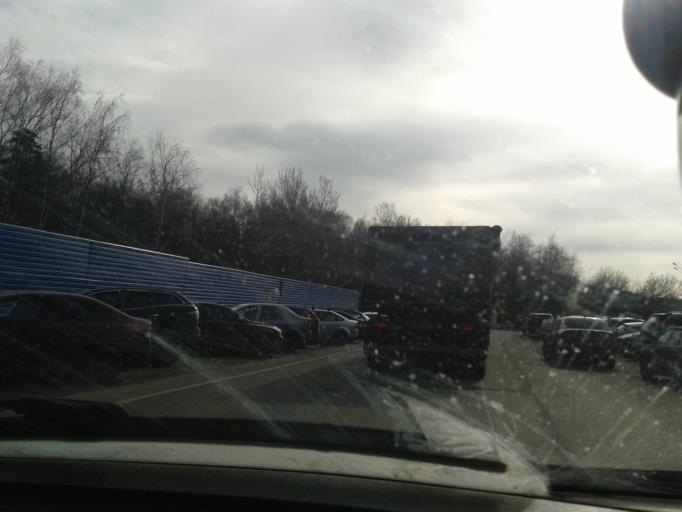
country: RU
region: Moscow
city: Lianozovo
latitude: 55.9152
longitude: 37.5902
